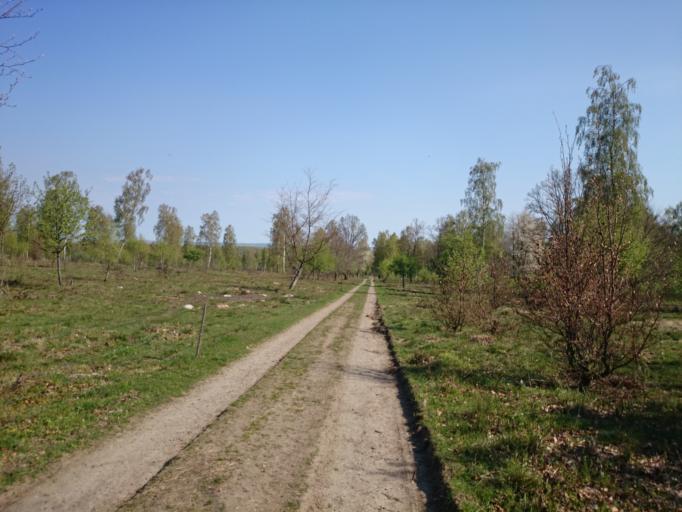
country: SE
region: Skane
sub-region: Lunds Kommun
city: Genarp
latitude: 55.6611
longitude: 13.3967
